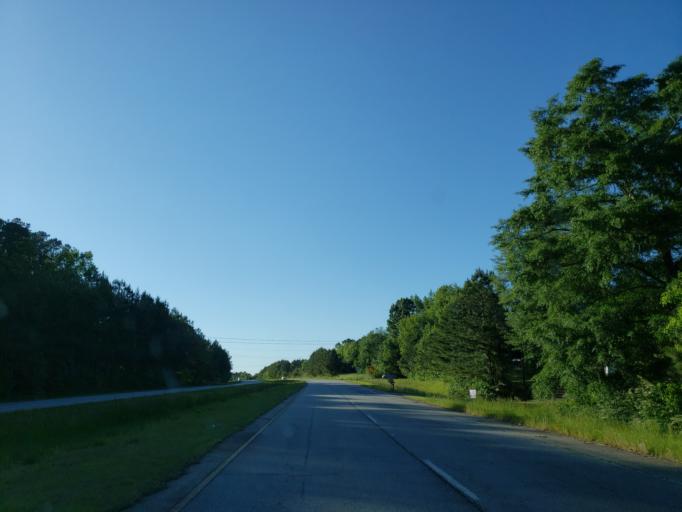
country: US
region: Georgia
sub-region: Haralson County
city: Buchanan
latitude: 33.9048
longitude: -85.2360
